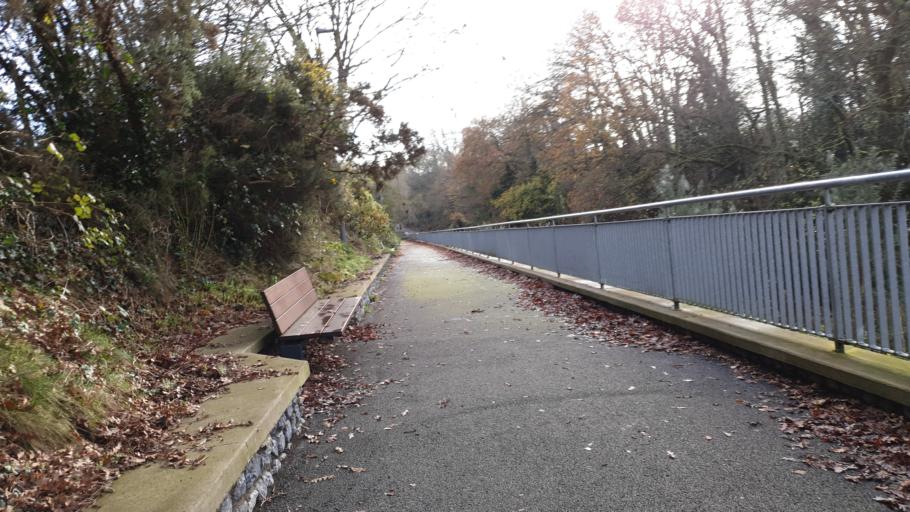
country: IE
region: Munster
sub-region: County Cork
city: Passage West
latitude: 51.8859
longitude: -8.4067
